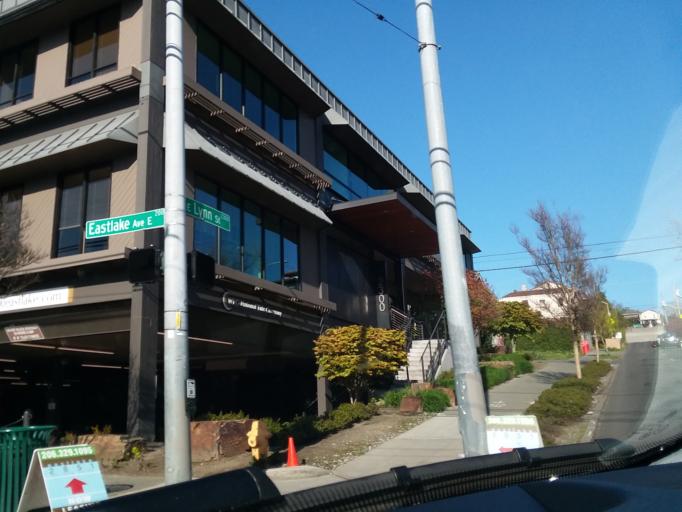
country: US
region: Washington
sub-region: King County
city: Seattle
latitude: 47.6398
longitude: -122.3259
